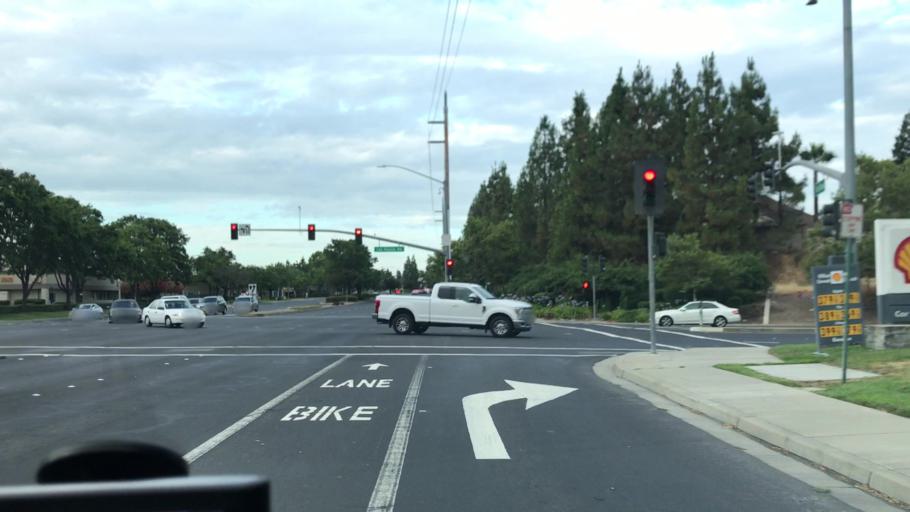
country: US
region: California
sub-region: Alameda County
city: Livermore
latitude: 37.6988
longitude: -121.7428
